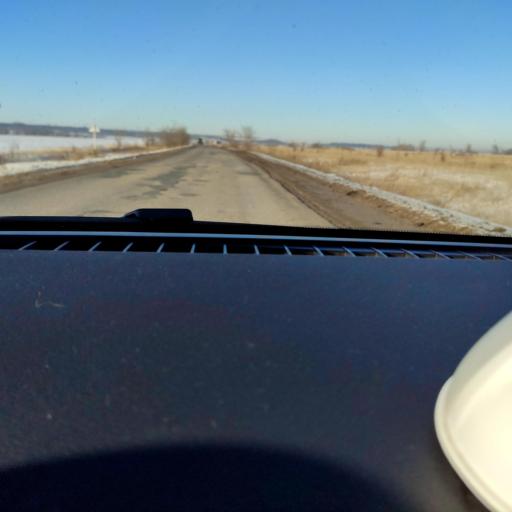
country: RU
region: Samara
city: Spiridonovka
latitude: 53.1237
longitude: 50.6284
